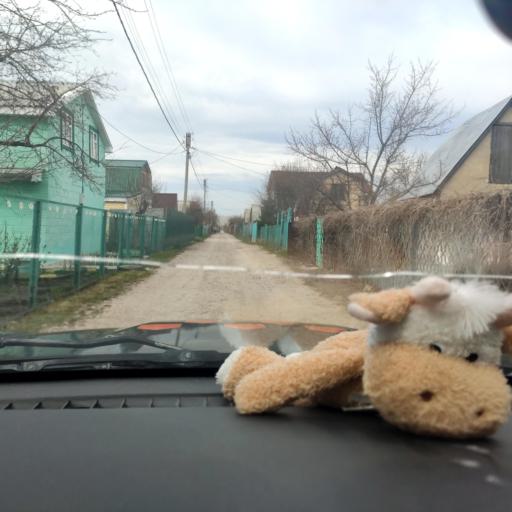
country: RU
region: Samara
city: Tol'yatti
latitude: 53.5978
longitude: 49.2396
